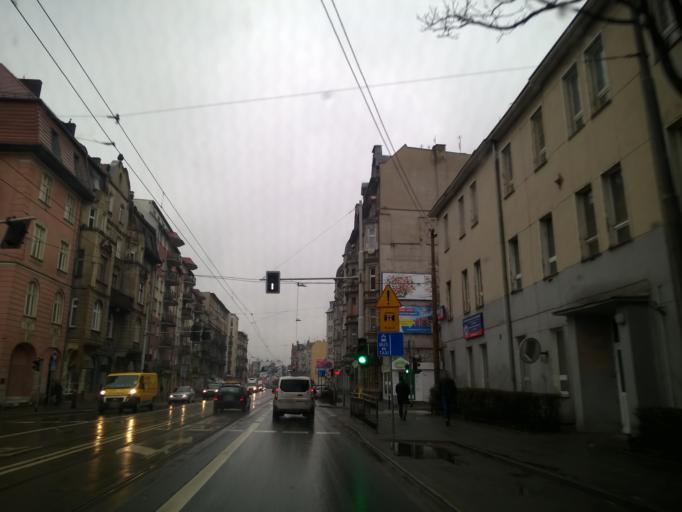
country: PL
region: Lower Silesian Voivodeship
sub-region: Powiat wroclawski
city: Wroclaw
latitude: 51.1003
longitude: 17.0538
